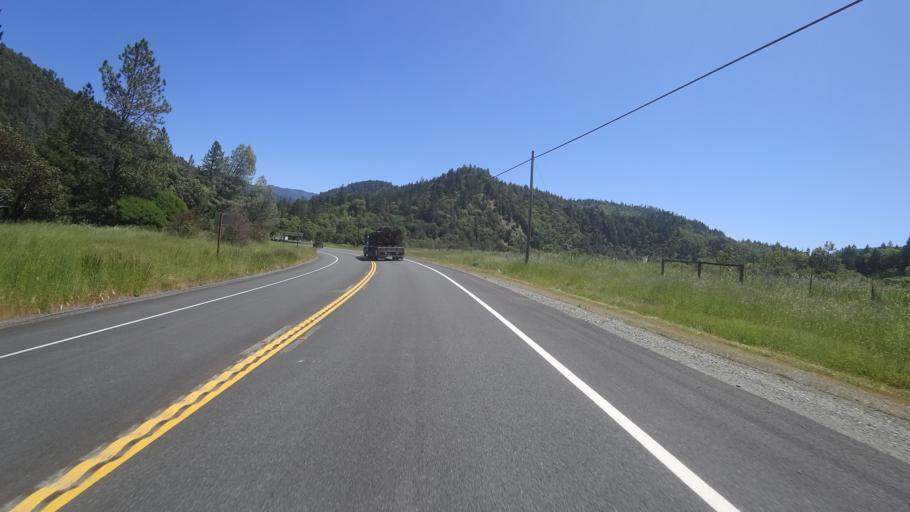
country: US
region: California
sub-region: Humboldt County
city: Willow Creek
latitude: 40.8879
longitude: -123.6041
